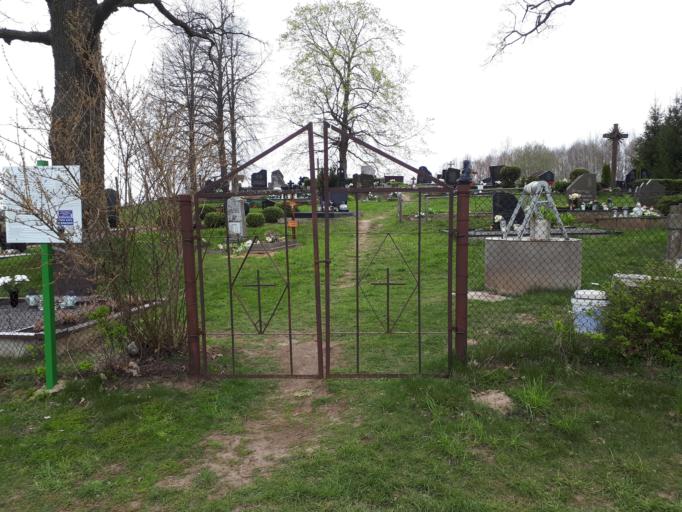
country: LT
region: Alytaus apskritis
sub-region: Alytaus rajonas
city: Daugai
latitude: 54.4303
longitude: 24.3183
